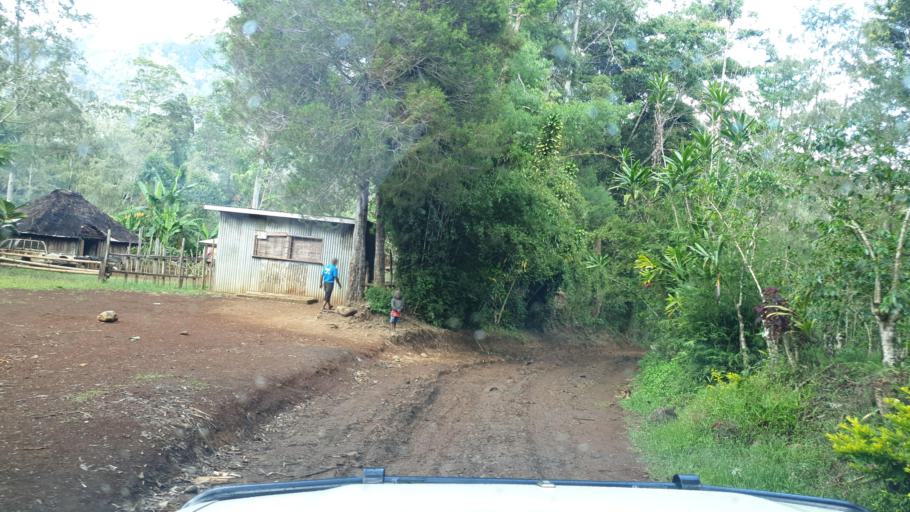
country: PG
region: Eastern Highlands
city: Goroka
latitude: -5.9201
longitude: 145.2602
